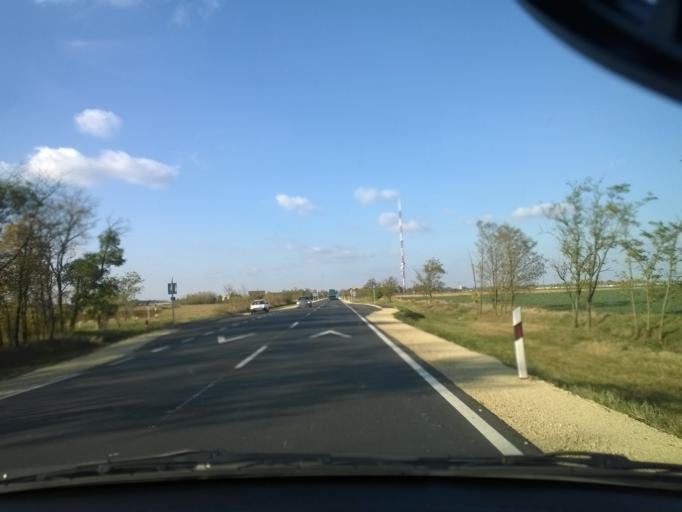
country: HU
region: Csongrad
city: Szentes
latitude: 46.6130
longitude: 20.2876
